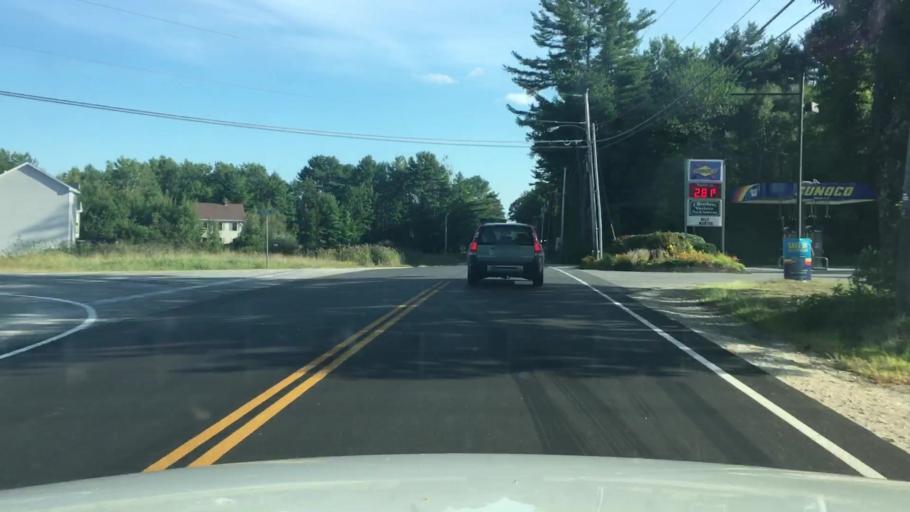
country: US
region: Maine
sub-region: Cumberland County
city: Cumberland Center
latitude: 43.7976
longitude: -70.3065
